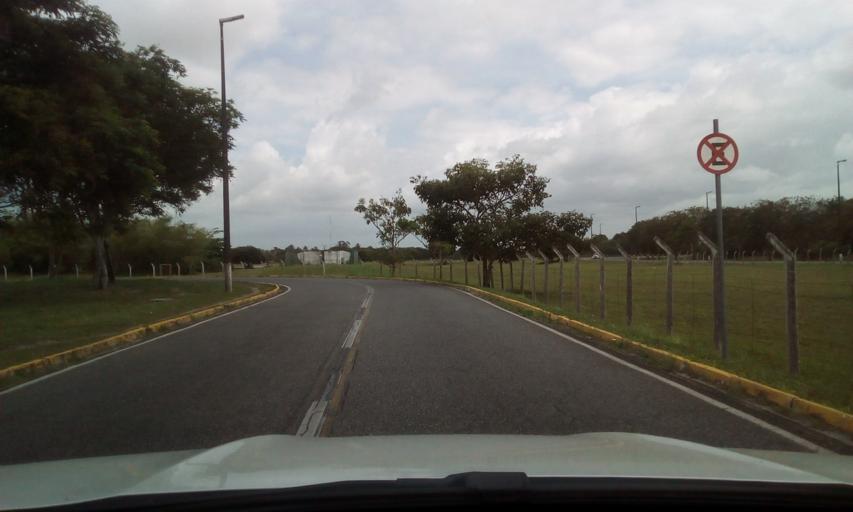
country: BR
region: Paraiba
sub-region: Bayeux
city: Bayeux
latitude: -7.1441
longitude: -34.9484
